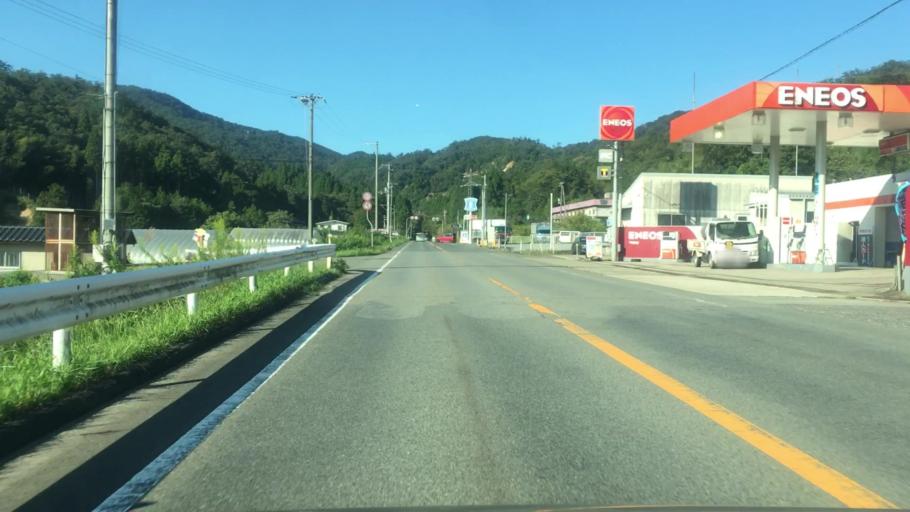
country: JP
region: Hyogo
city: Toyooka
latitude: 35.5599
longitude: 134.8513
